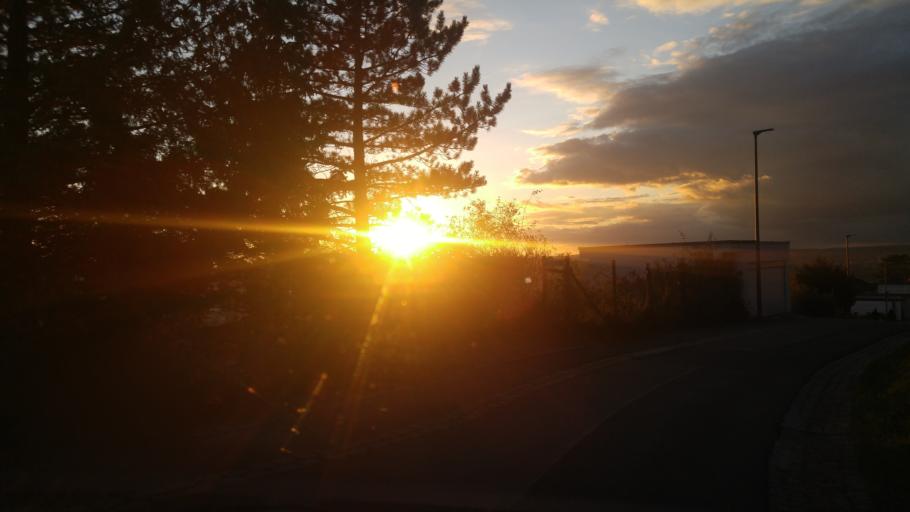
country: DE
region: Baden-Wuerttemberg
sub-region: Regierungsbezirk Stuttgart
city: Leonberg
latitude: 48.7989
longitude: 9.0262
